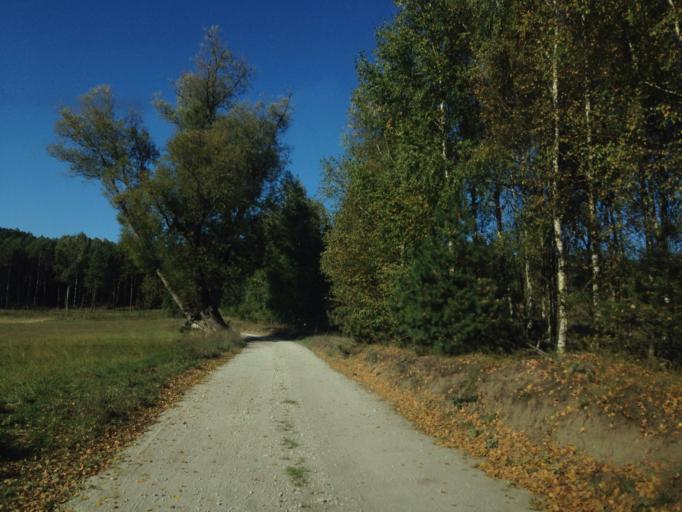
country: PL
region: Kujawsko-Pomorskie
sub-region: Powiat brodnicki
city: Gorzno
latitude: 53.2317
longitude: 19.7004
